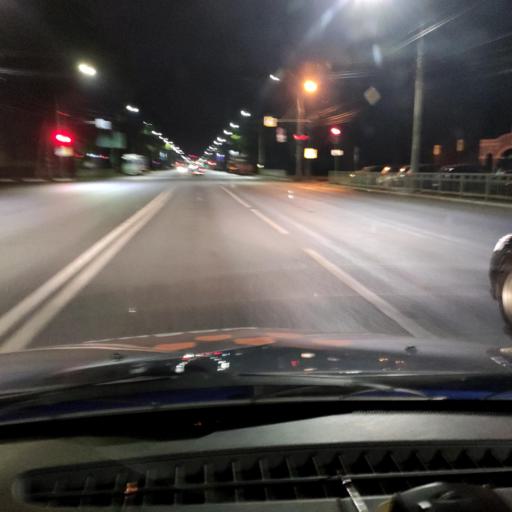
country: RU
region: Voronezj
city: Voronezh
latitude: 51.6471
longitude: 39.2395
